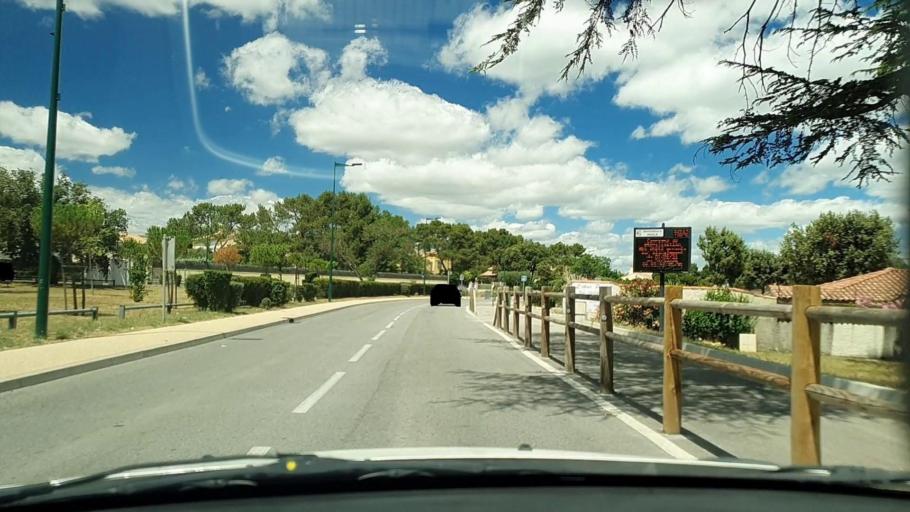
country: FR
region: Languedoc-Roussillon
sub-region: Departement du Gard
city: Poulx
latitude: 43.9003
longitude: 4.4214
